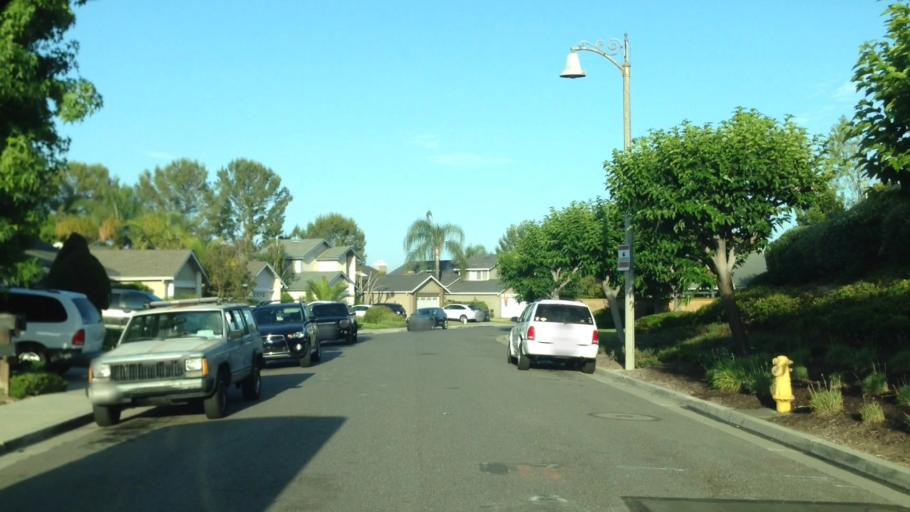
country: US
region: California
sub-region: Orange County
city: Rancho Santa Margarita
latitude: 33.6455
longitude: -117.6296
